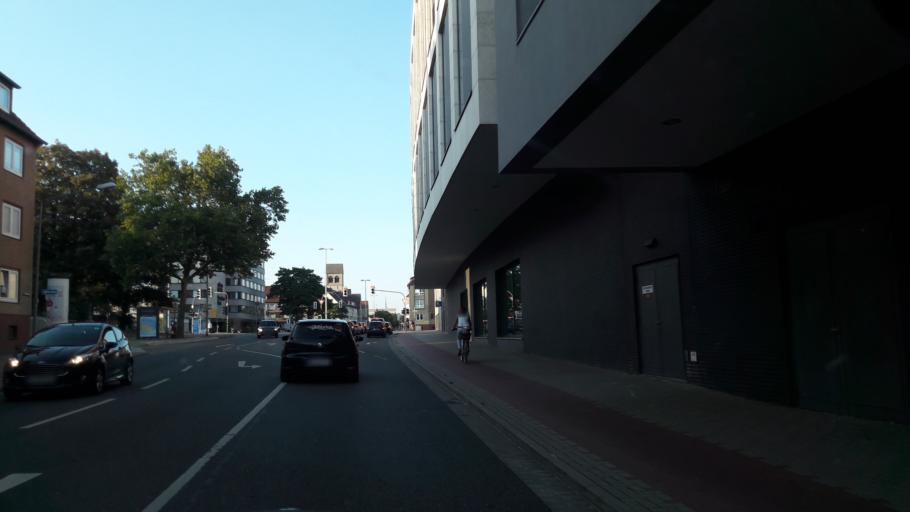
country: DE
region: Lower Saxony
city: Hildesheim
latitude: 52.1539
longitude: 9.9485
